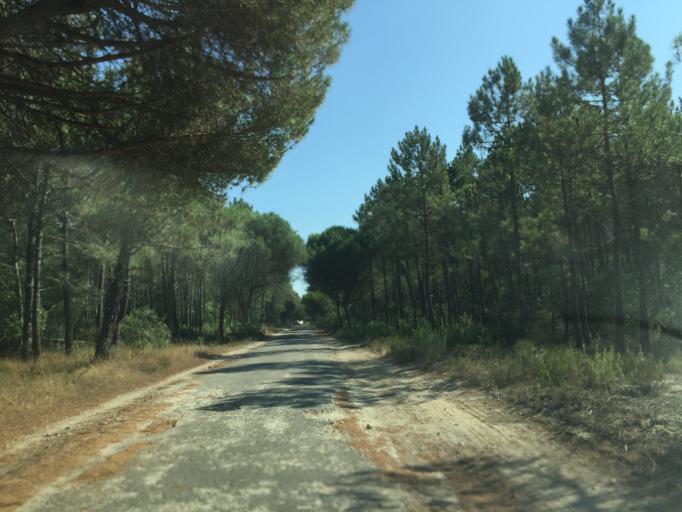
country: PT
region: Coimbra
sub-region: Figueira da Foz
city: Tavarede
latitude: 40.2326
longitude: -8.8483
